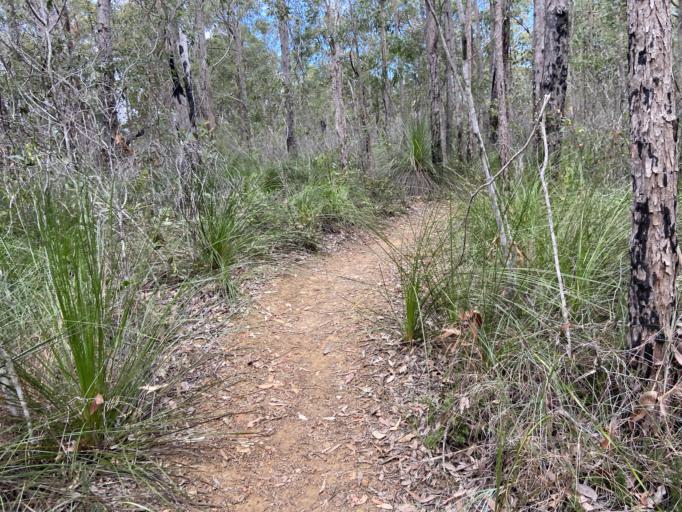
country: AU
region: Queensland
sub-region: Moreton Bay
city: Caboolture
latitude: -26.9460
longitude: 152.9506
